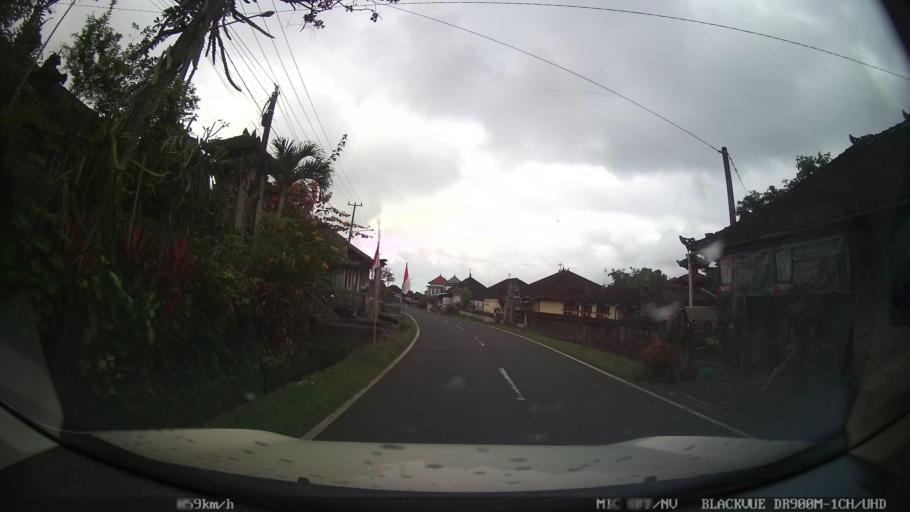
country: ID
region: Bali
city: Empalan
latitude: -8.3945
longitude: 115.1513
